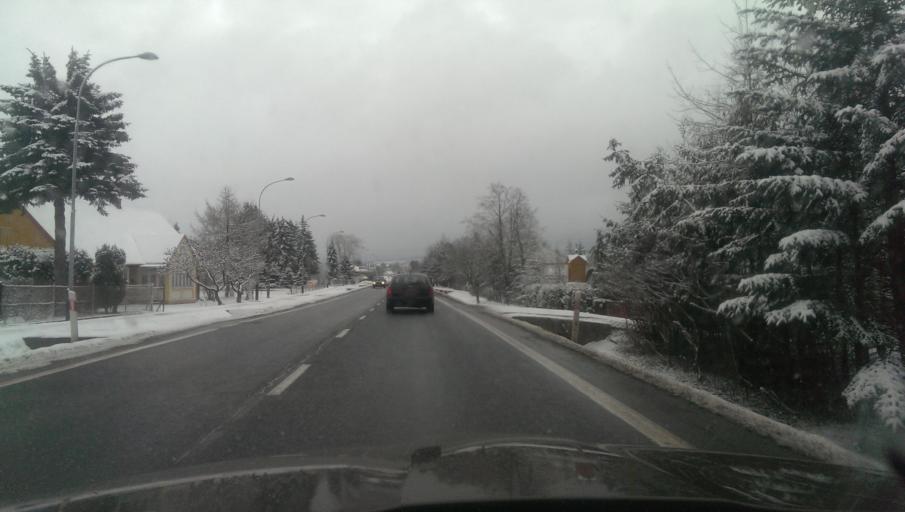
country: PL
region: Subcarpathian Voivodeship
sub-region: Powiat krosnienski
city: Miejsce Piastowe
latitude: 49.6096
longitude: 21.8032
